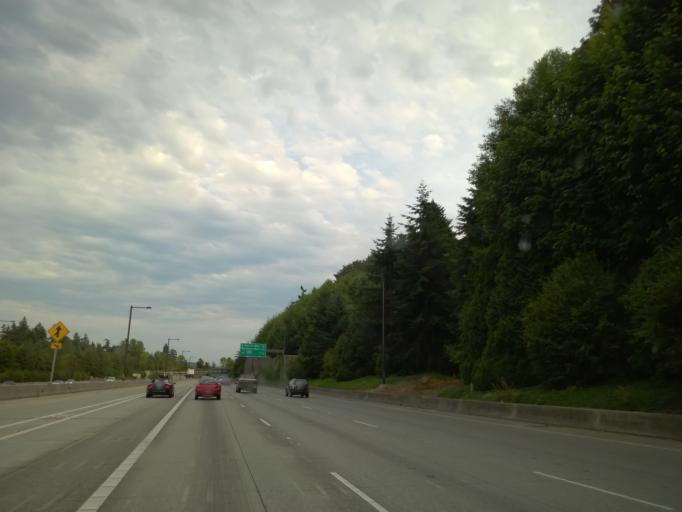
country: US
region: Washington
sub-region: King County
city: Mercer Island
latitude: 47.5841
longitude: -122.2240
